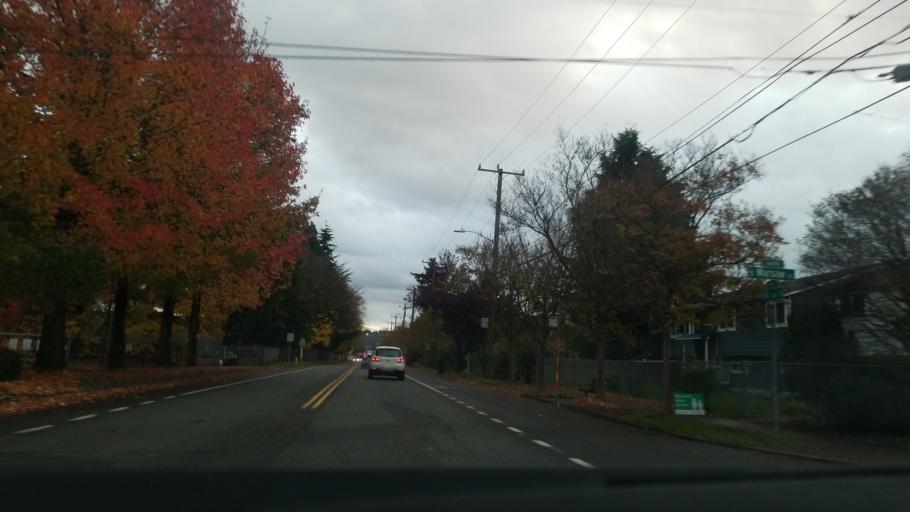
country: US
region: Washington
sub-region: King County
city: White Center
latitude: 47.5443
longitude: -122.3187
